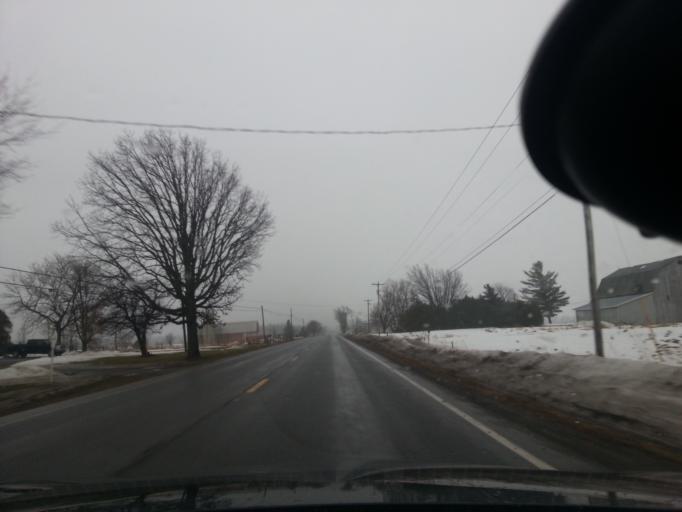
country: US
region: New York
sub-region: St. Lawrence County
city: Ogdensburg
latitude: 44.6360
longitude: -75.4285
